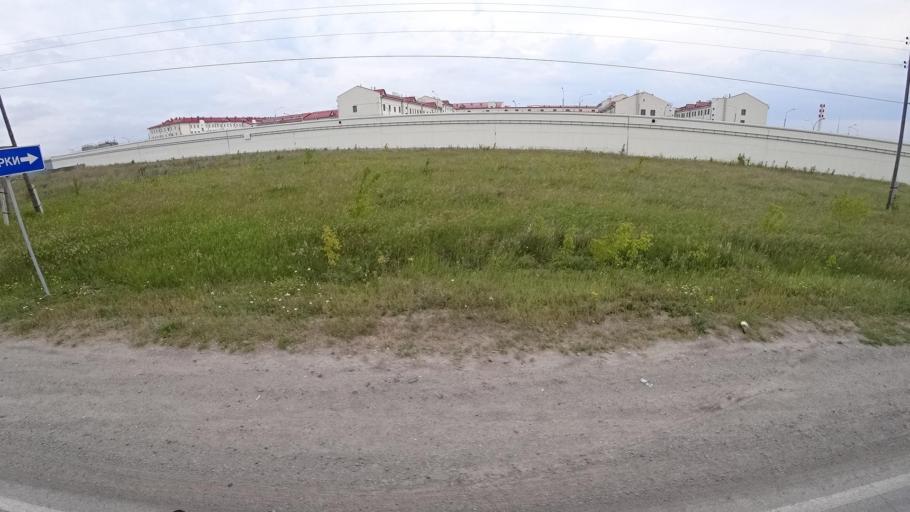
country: RU
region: Sverdlovsk
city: Kamyshlov
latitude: 56.8559
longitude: 62.7347
